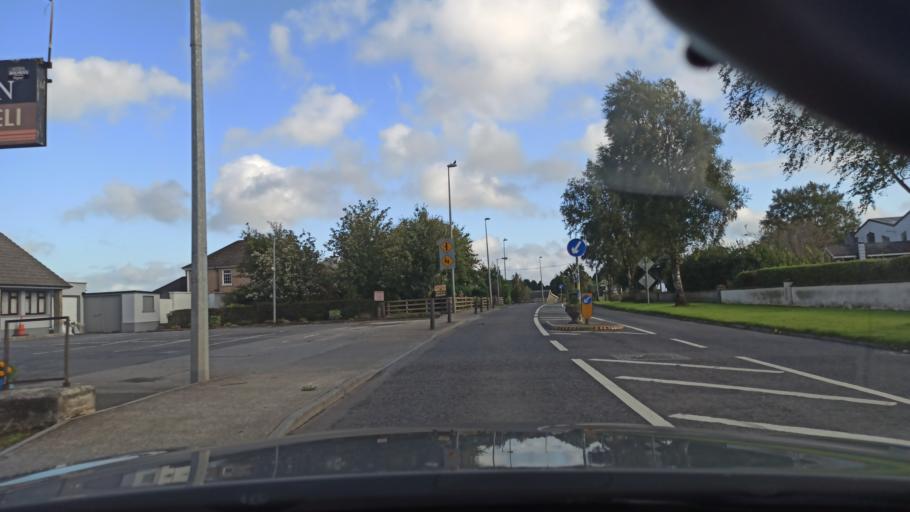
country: IE
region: Munster
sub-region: North Tipperary
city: Roscrea
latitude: 52.9401
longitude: -7.7882
